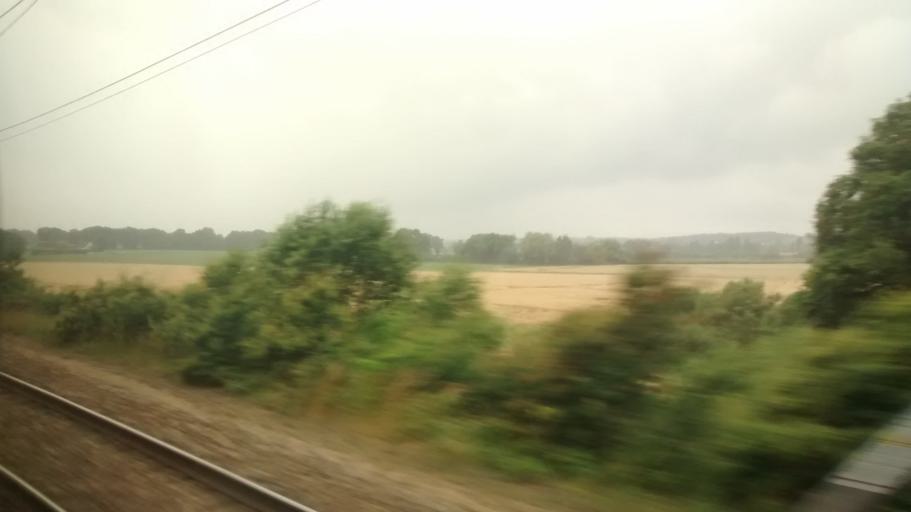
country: FR
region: Pays de la Loire
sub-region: Departement de la Sarthe
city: Vibraye
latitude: 48.0823
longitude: 0.7955
